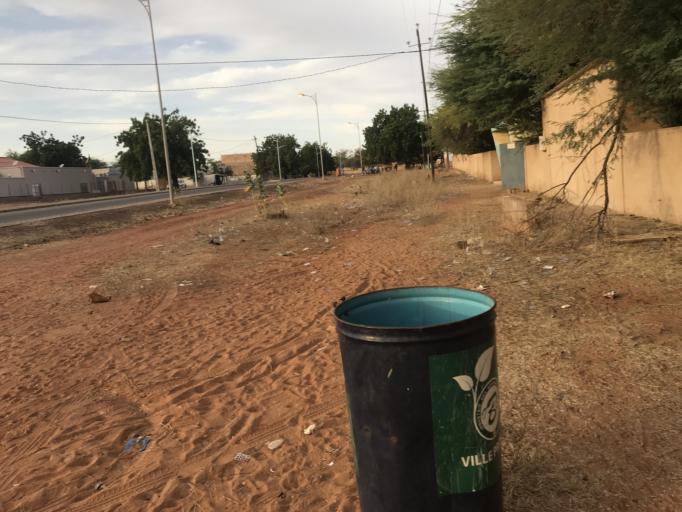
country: SN
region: Louga
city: Ndibene Dahra
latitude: 15.3996
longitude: -15.1130
